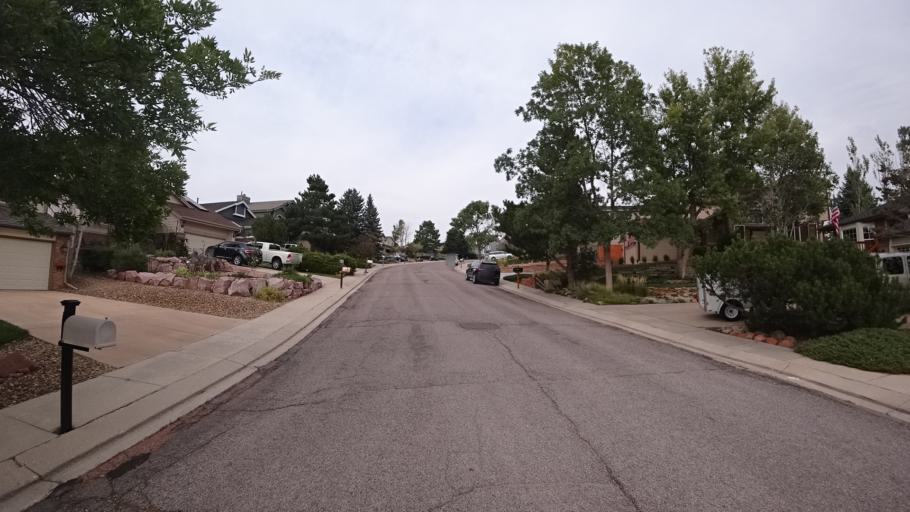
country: US
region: Colorado
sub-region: El Paso County
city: Cimarron Hills
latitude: 38.9077
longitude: -104.7294
